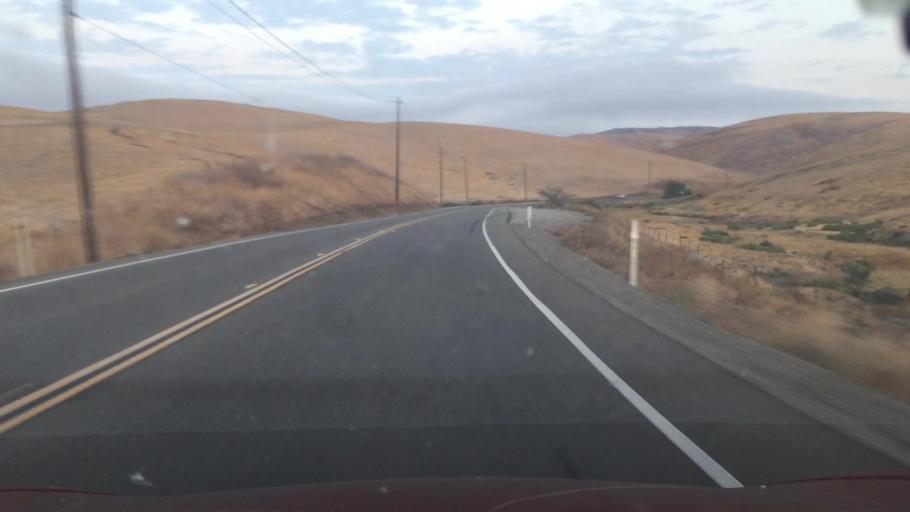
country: US
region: California
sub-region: San Joaquin County
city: Mountain House
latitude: 37.7413
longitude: -121.6218
